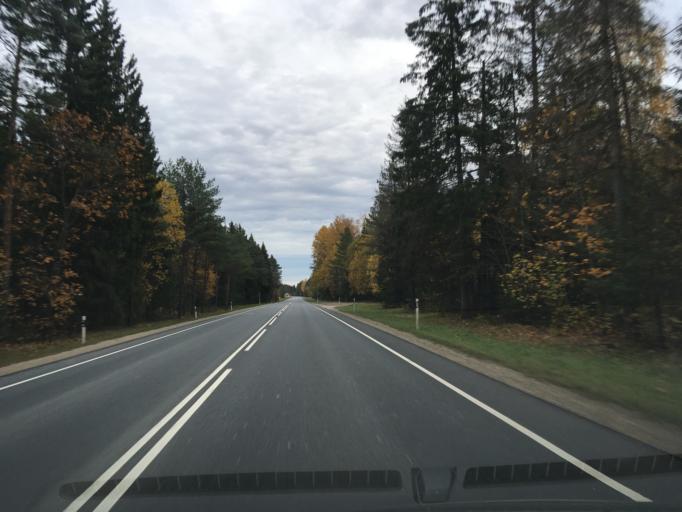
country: EE
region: Harju
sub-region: Nissi vald
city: Turba
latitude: 59.0310
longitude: 24.1571
